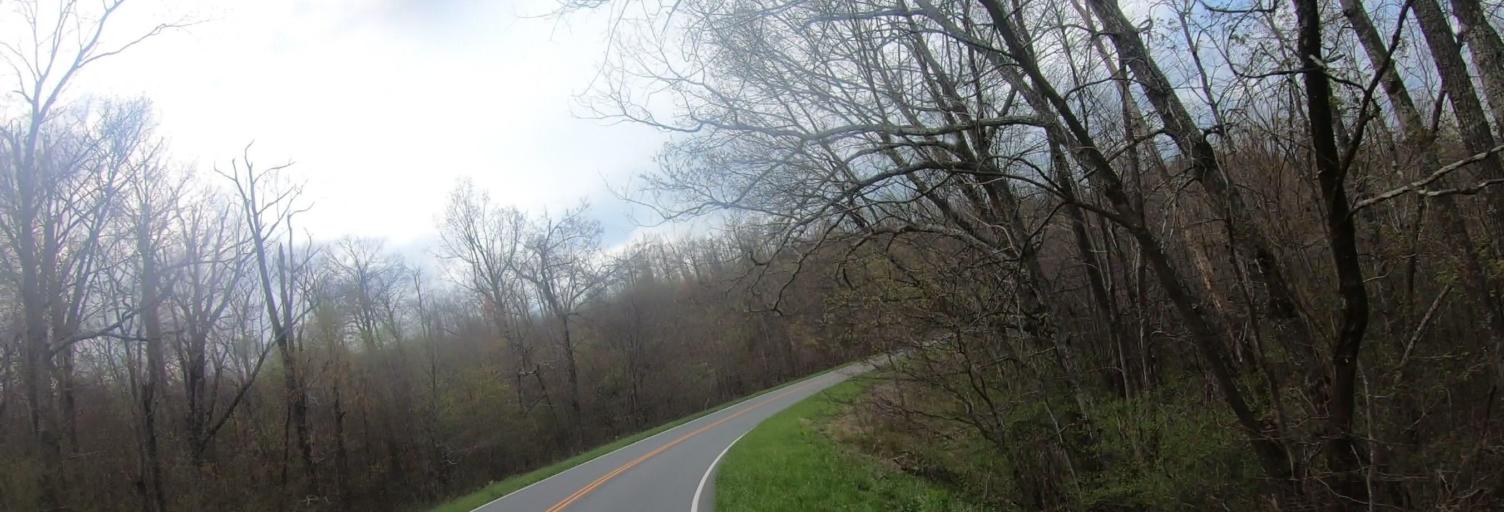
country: US
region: Virginia
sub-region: Rockingham County
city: Grottoes
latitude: 38.2127
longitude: -78.7378
